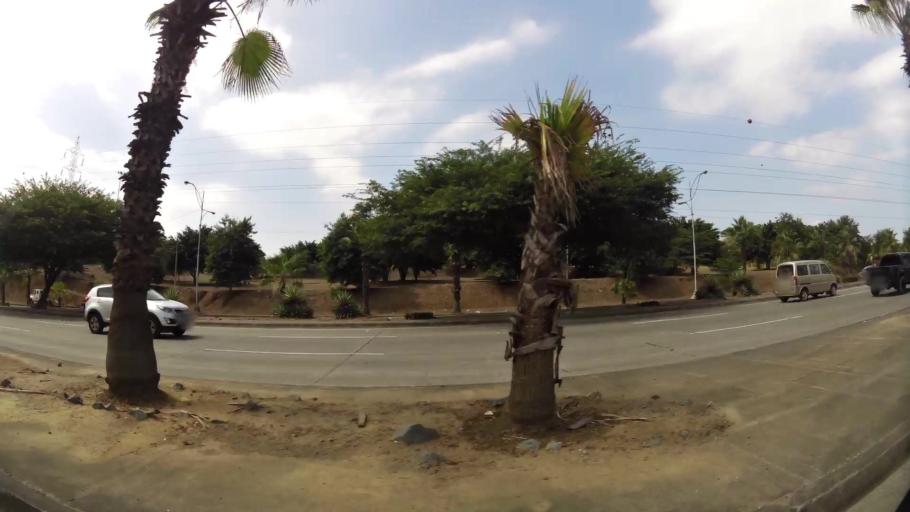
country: EC
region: Guayas
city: Eloy Alfaro
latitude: -2.0772
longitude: -79.9174
